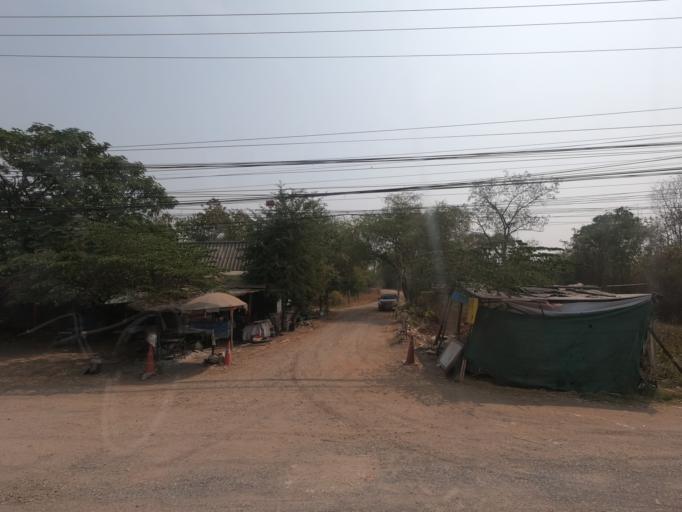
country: TH
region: Nakhon Ratchasima
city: Sida
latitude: 15.5449
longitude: 102.5476
